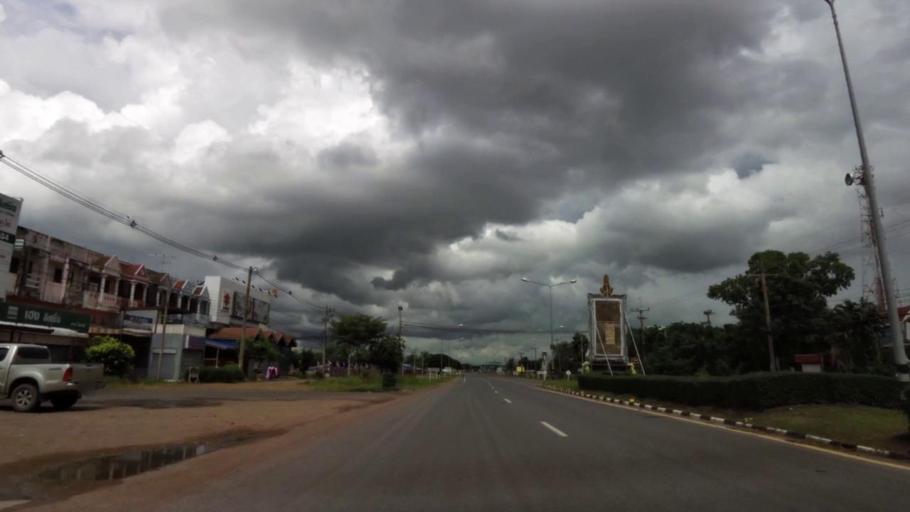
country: TH
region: Nakhon Sawan
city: Phai Sali
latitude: 15.5946
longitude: 100.6566
